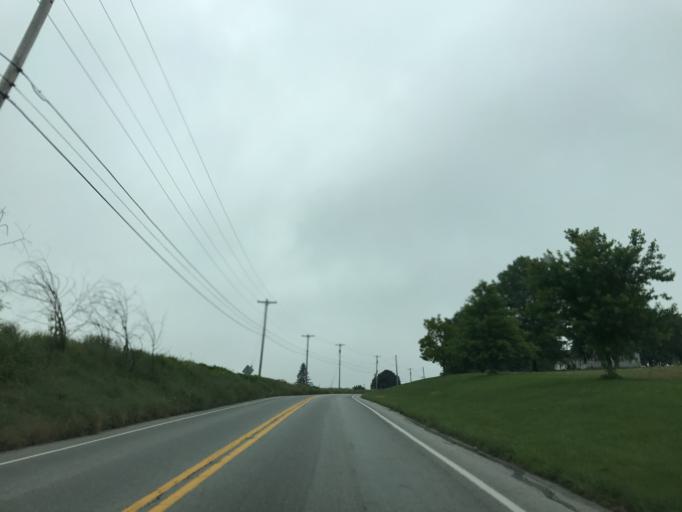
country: US
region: Pennsylvania
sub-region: York County
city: Susquehanna Trails
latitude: 39.8352
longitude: -76.4115
